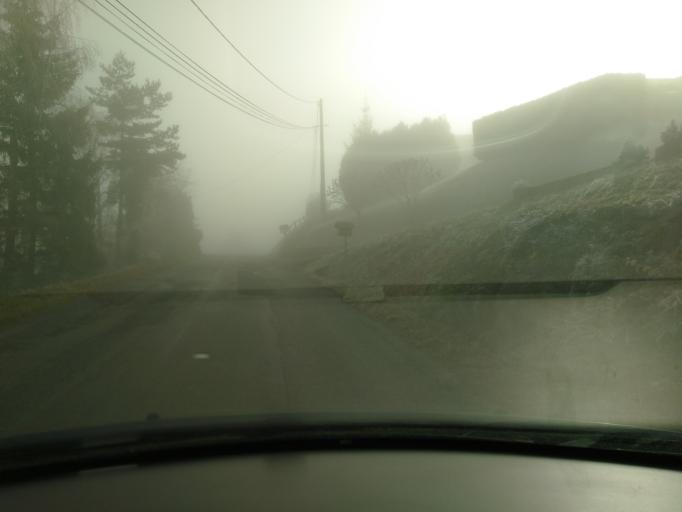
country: FR
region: Rhone-Alpes
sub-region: Departement de la Haute-Savoie
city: Sallanches
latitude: 45.9648
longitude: 6.6155
